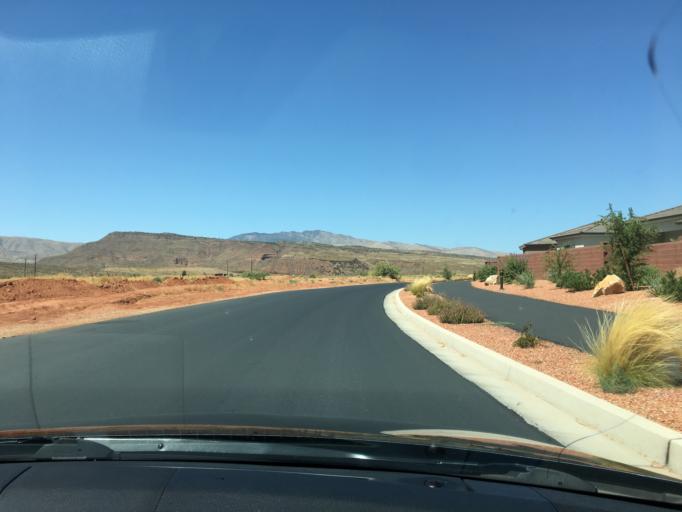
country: US
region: Utah
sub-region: Washington County
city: Ivins
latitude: 37.1608
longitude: -113.6921
